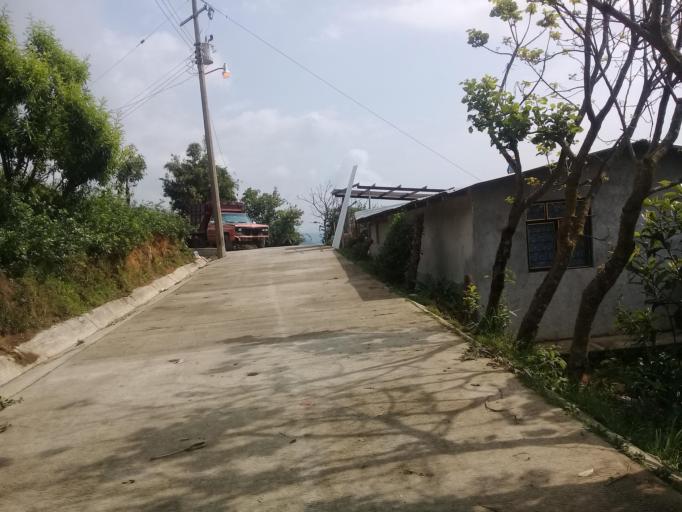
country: MX
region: Veracruz
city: La Perla
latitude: 18.9433
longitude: -97.1579
